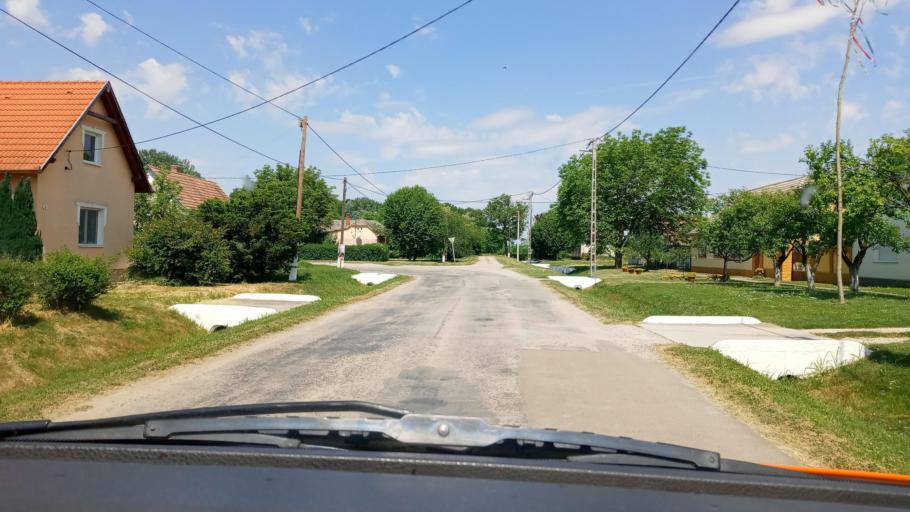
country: HR
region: Osjecko-Baranjska
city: Viljevo
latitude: 45.8157
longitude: 18.1187
